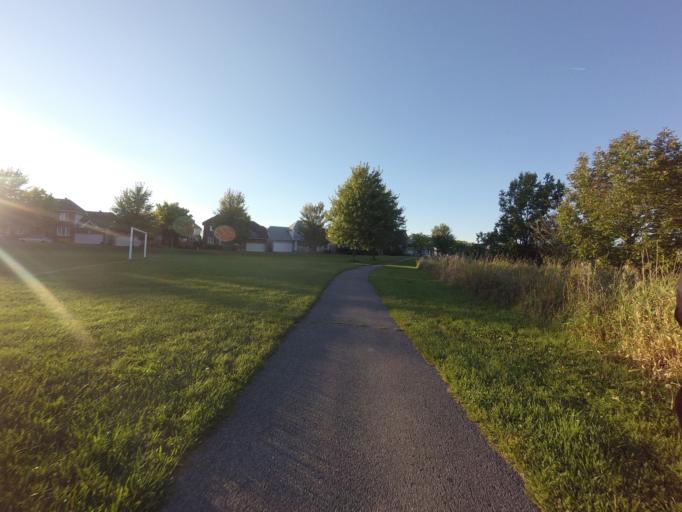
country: CA
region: Ontario
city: Bells Corners
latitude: 45.2790
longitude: -75.7056
